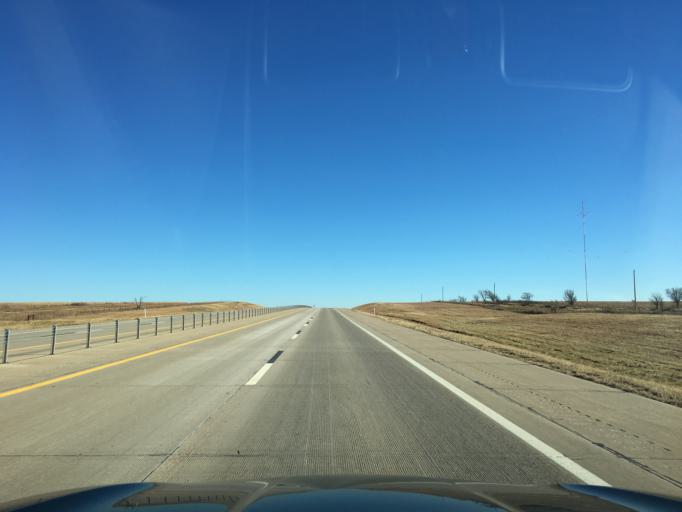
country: US
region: Oklahoma
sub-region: Noble County
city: Perry
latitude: 36.3920
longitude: -97.1553
